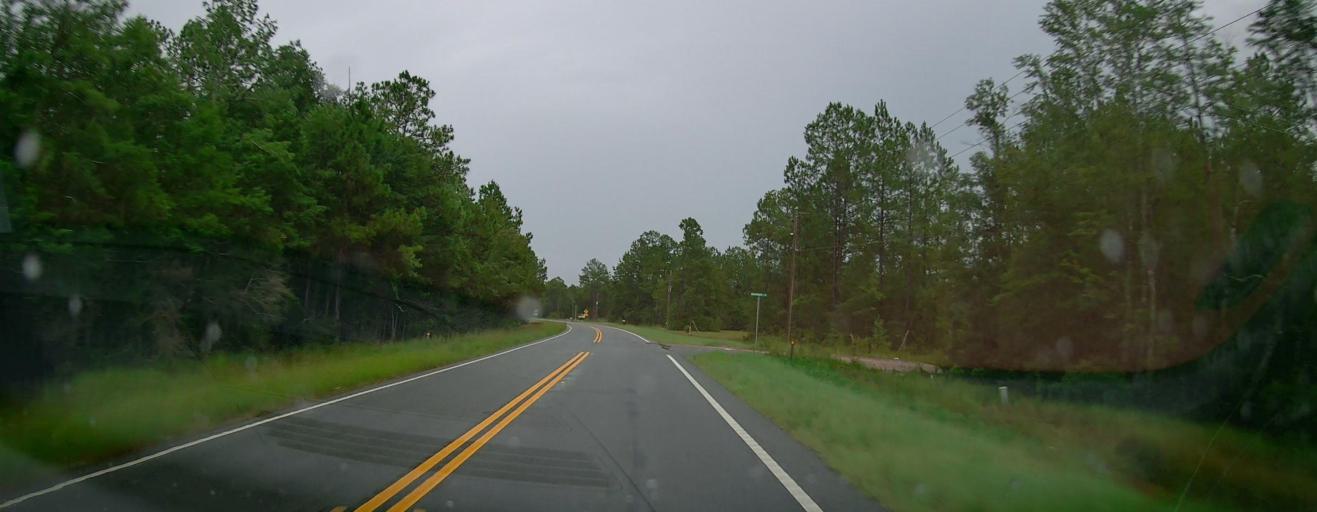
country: US
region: Georgia
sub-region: Brantley County
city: Nahunta
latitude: 31.3308
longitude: -81.9264
